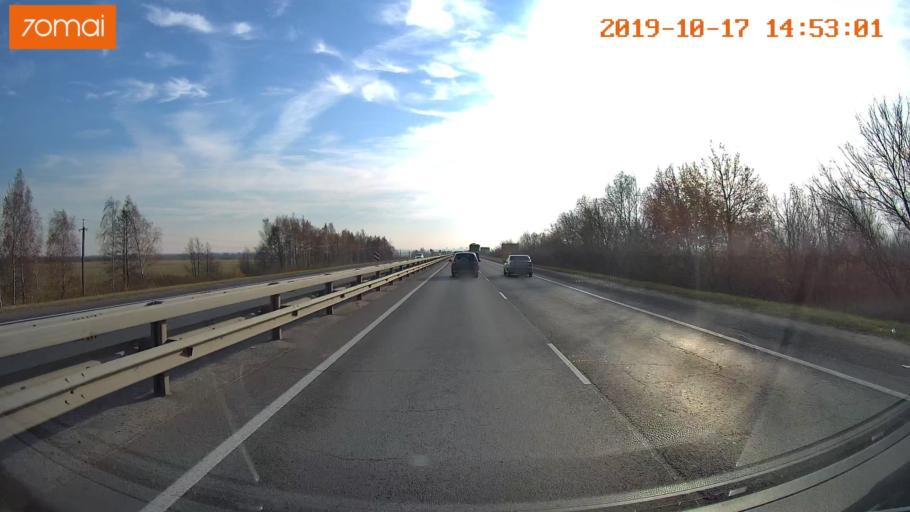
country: RU
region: Rjazan
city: Polyany
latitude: 54.6998
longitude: 39.8416
